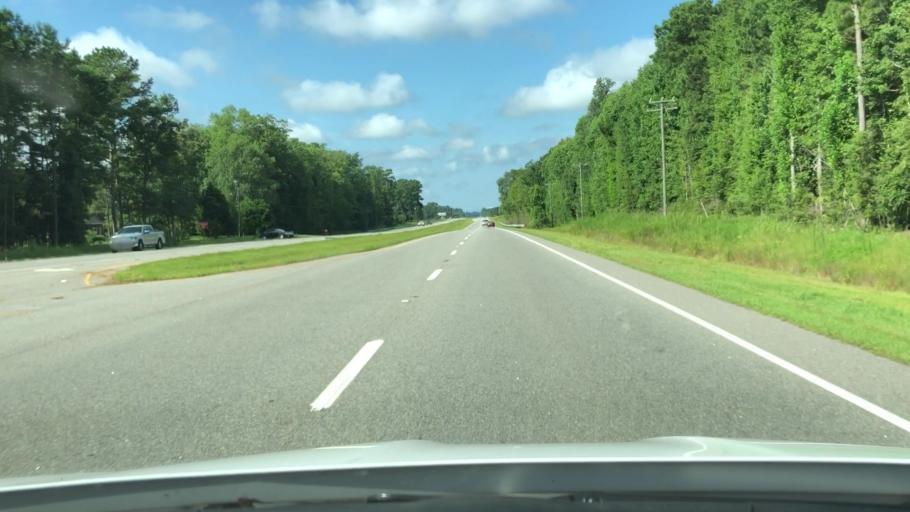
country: US
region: North Carolina
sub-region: Perquimans County
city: Hertford
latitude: 36.1293
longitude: -76.4980
